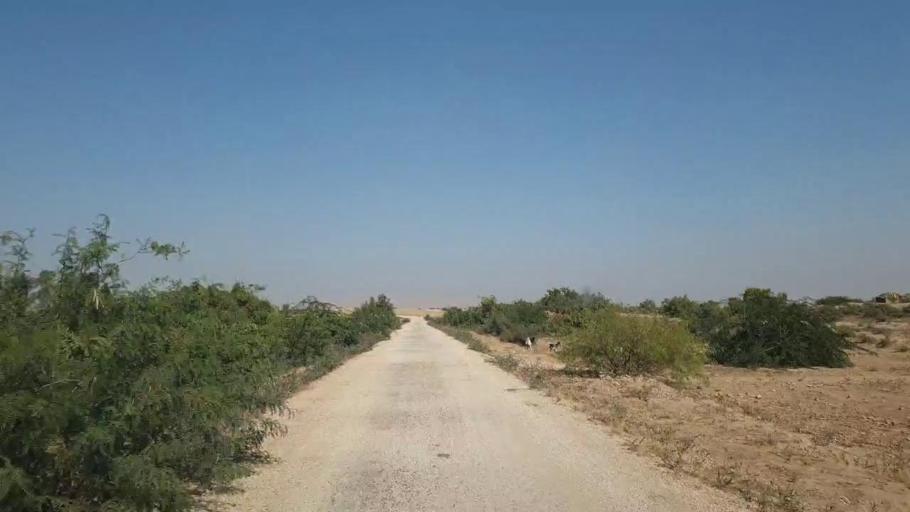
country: PK
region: Sindh
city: Jamshoro
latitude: 25.4835
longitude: 67.8386
